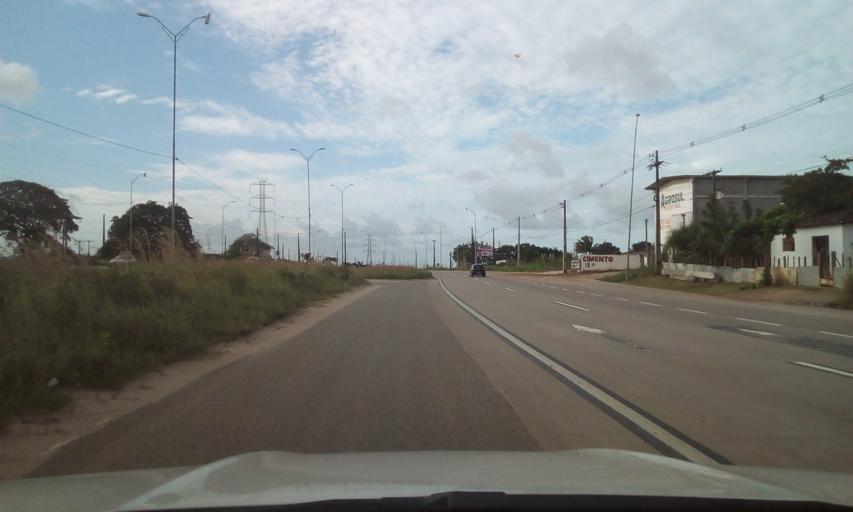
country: BR
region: Paraiba
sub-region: Conde
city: Conde
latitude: -7.2585
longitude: -34.9354
